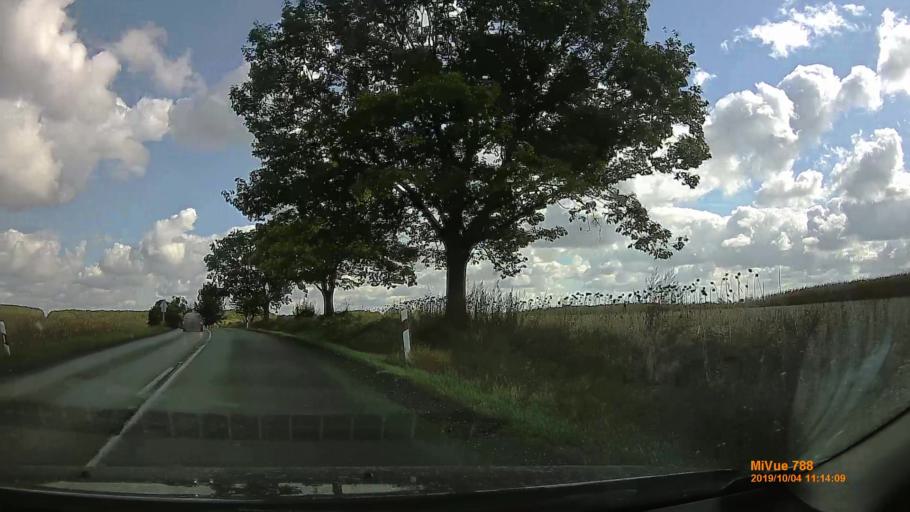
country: HU
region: Somogy
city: Kaposvar
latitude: 46.4352
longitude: 17.7891
